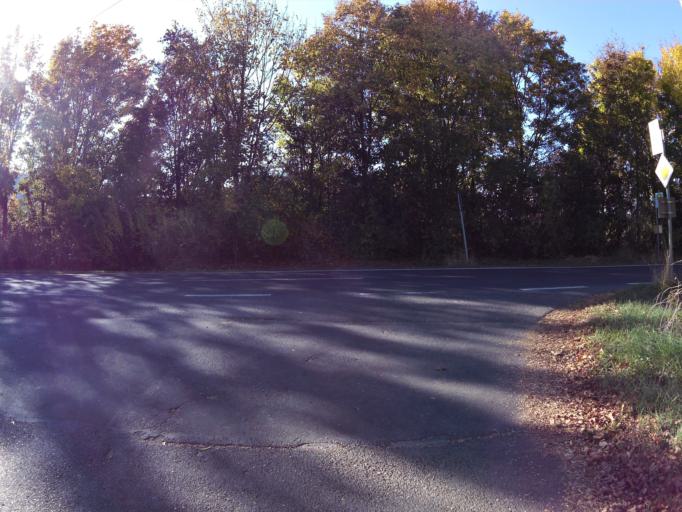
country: DE
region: Bavaria
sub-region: Regierungsbezirk Unterfranken
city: Eibelstadt
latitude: 49.7109
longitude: 9.9634
